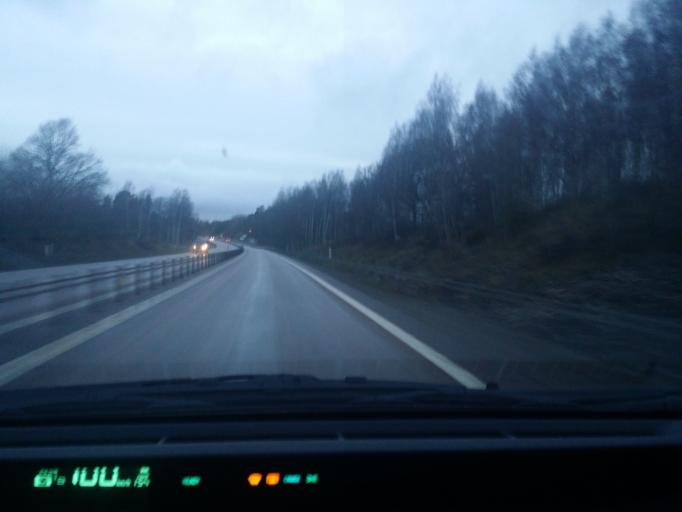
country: SE
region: Soedermanland
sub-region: Eskilstuna Kommun
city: Kvicksund
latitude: 59.4416
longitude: 16.3469
